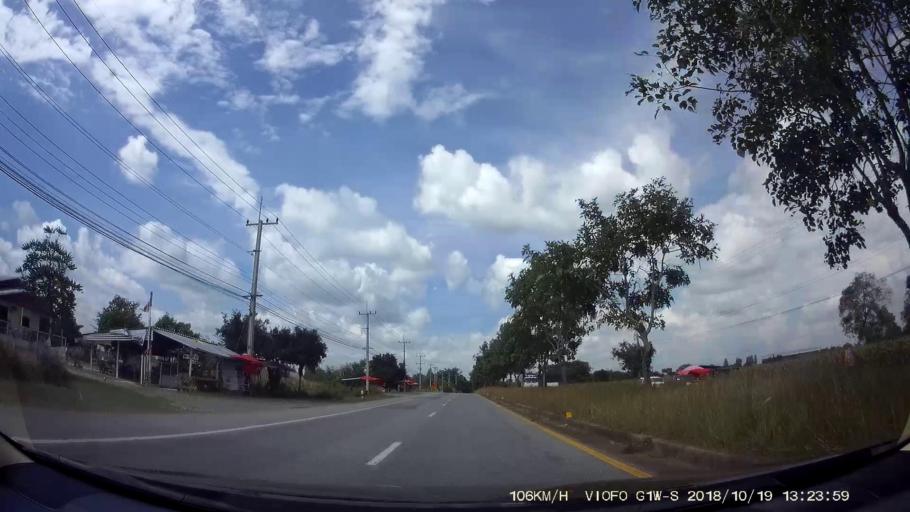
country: TH
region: Chaiyaphum
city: Chatturat
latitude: 15.5008
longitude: 101.8202
